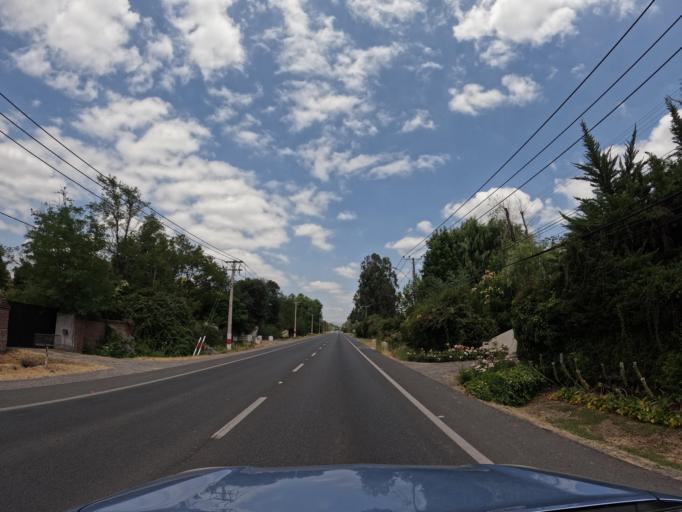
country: CL
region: Maule
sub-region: Provincia de Curico
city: Curico
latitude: -35.0102
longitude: -71.2200
